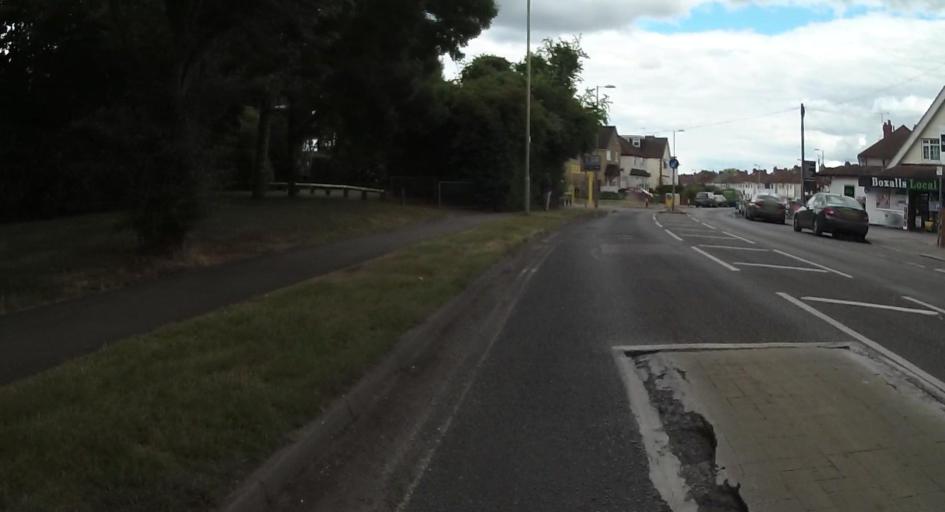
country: GB
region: England
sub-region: Hampshire
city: Aldershot
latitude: 51.2368
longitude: -0.7624
